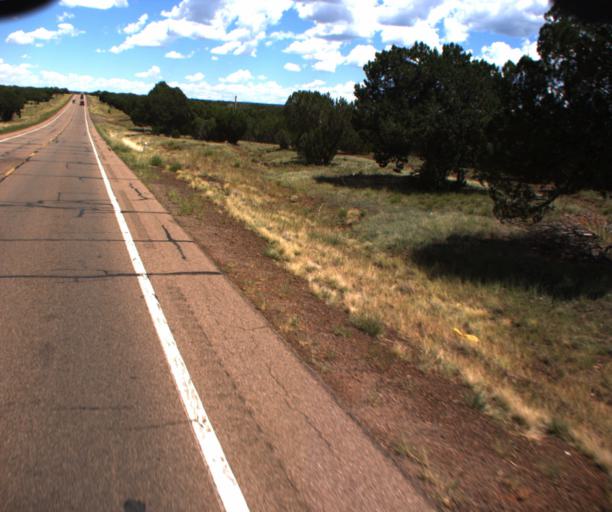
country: US
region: Arizona
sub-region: Navajo County
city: Show Low
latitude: 34.2654
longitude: -109.9542
